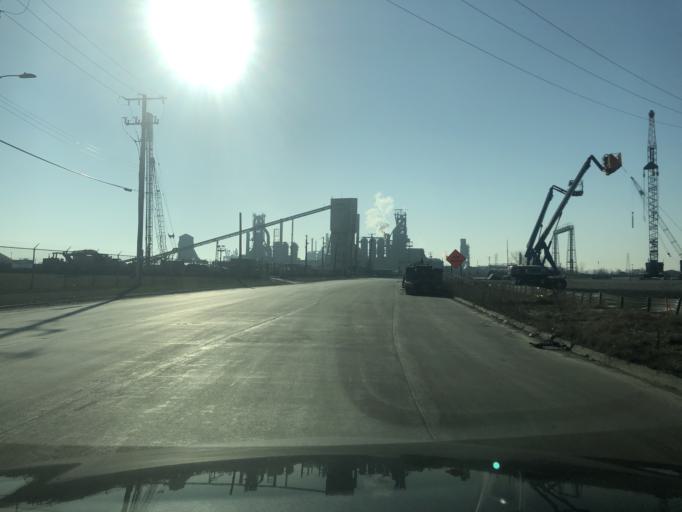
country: US
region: Michigan
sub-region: Wayne County
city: River Rouge
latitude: 42.2924
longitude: -83.1031
